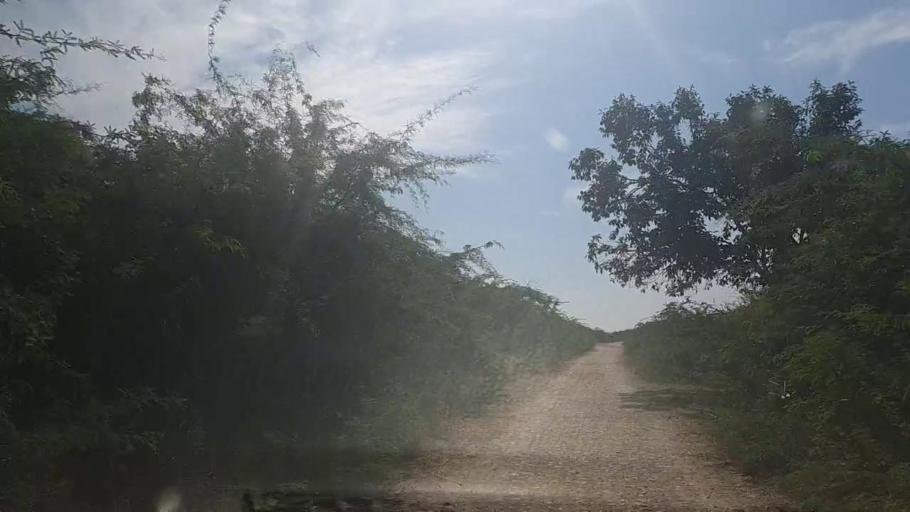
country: PK
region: Sindh
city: Mirpur Batoro
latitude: 24.6798
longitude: 68.1820
